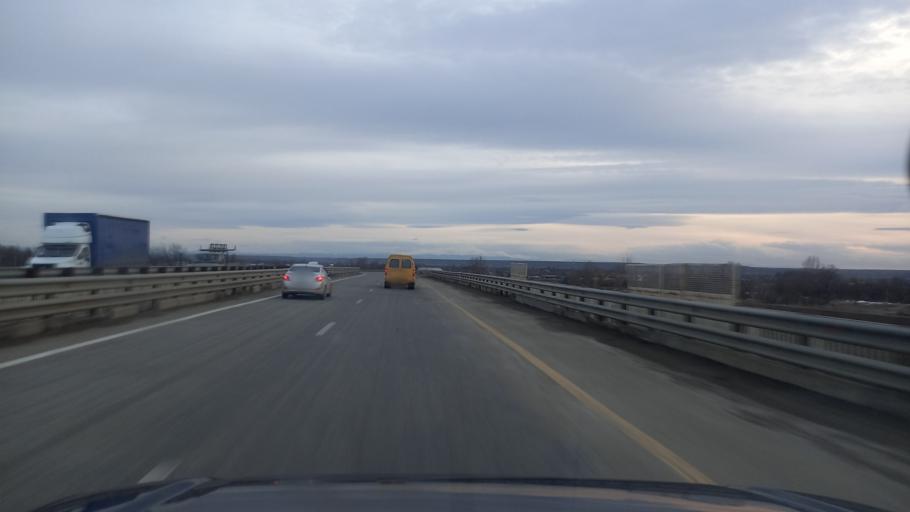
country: RU
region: Adygeya
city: Khanskaya
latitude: 44.6999
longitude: 39.9686
